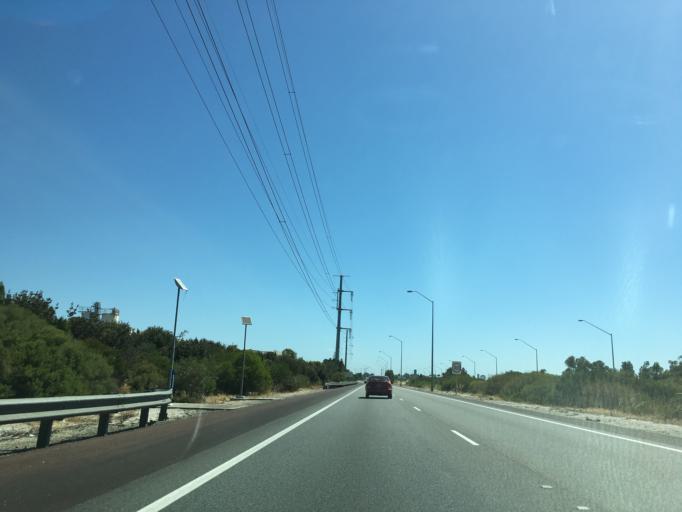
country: AU
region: Western Australia
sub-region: Canning
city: Willetton
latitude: -32.0627
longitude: 115.8980
